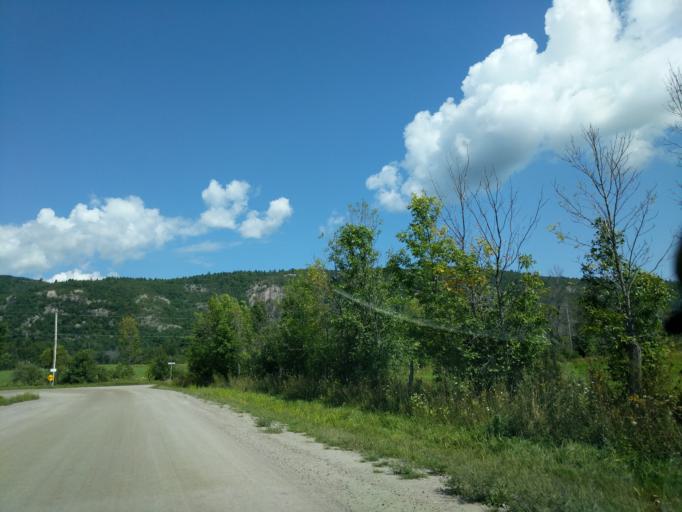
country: CA
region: Quebec
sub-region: Outaouais
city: Wakefield
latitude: 45.5172
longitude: -75.9552
